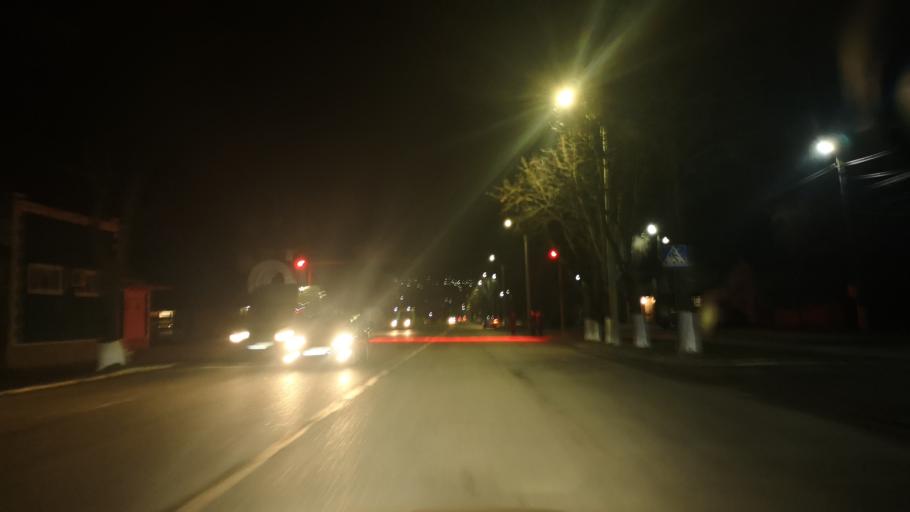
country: MD
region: Orhei
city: Orhei
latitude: 47.3621
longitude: 28.8122
